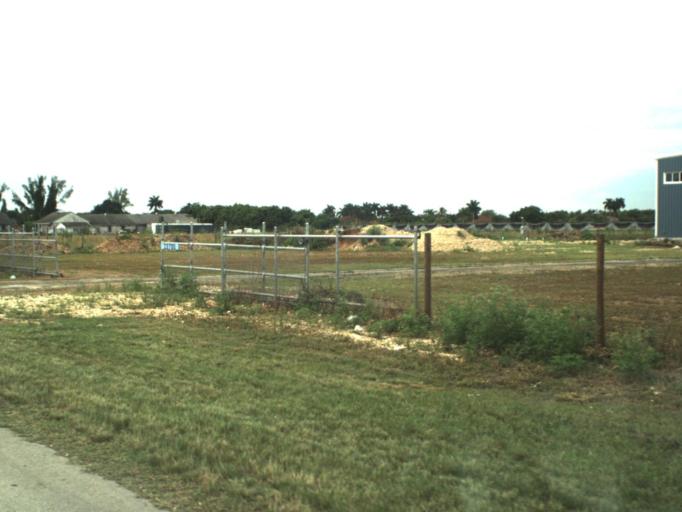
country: US
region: Florida
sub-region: Miami-Dade County
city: Naranja
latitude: 25.5549
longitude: -80.4782
